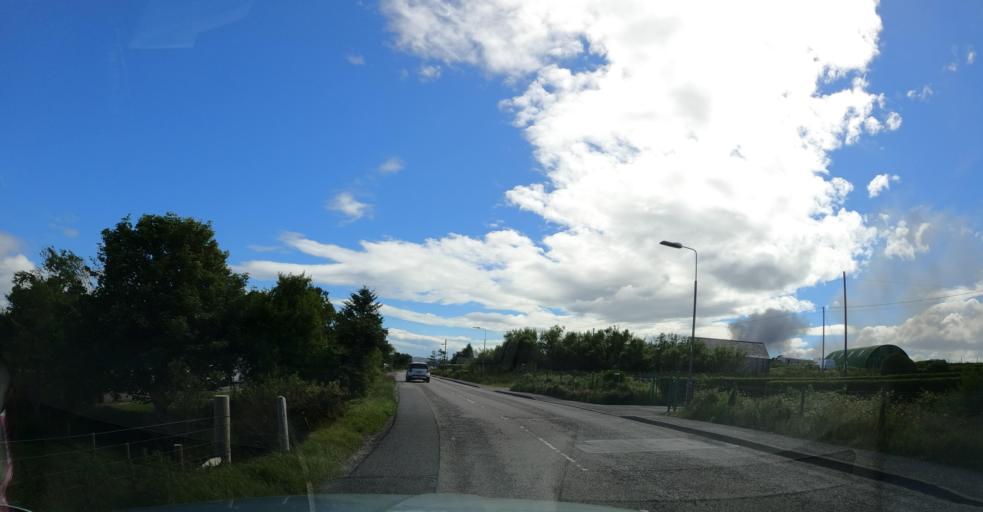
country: GB
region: Scotland
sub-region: Eilean Siar
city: Isle of Lewis
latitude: 58.2343
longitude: -6.3904
